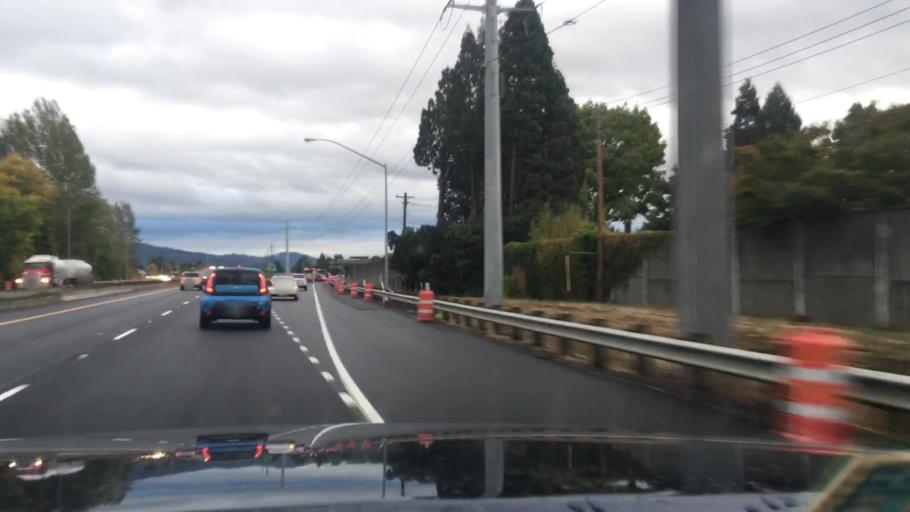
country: US
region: Oregon
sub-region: Lane County
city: Eugene
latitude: 44.0878
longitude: -123.0761
